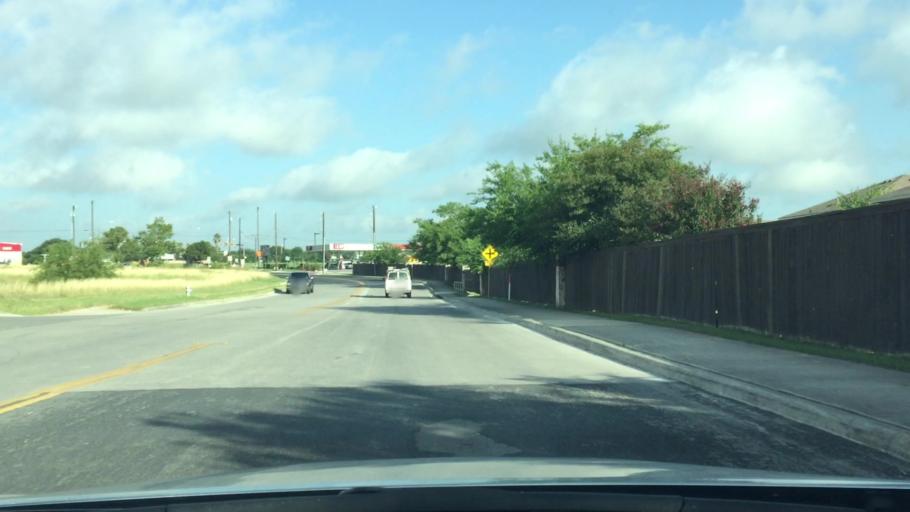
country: US
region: Texas
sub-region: Bexar County
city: Kirby
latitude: 29.4672
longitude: -98.3570
